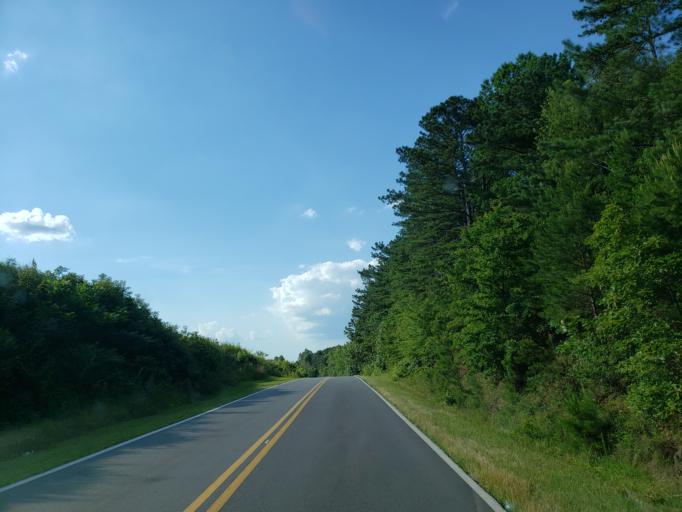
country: US
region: Georgia
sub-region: Haralson County
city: Bremen
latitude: 33.6955
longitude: -85.1355
